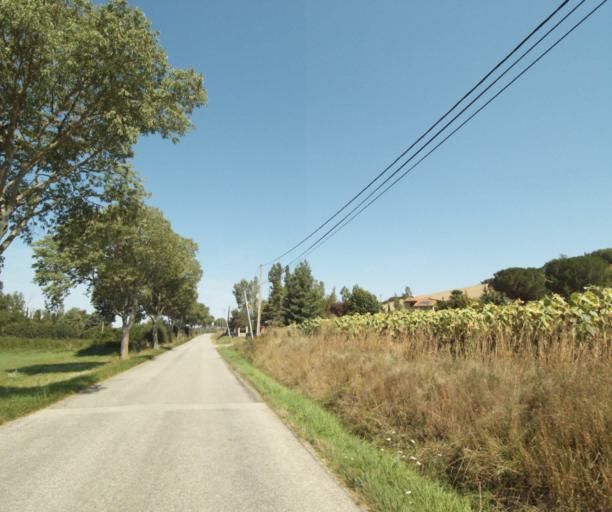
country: FR
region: Midi-Pyrenees
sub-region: Departement de l'Ariege
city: Lezat-sur-Leze
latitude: 43.2837
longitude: 1.3549
